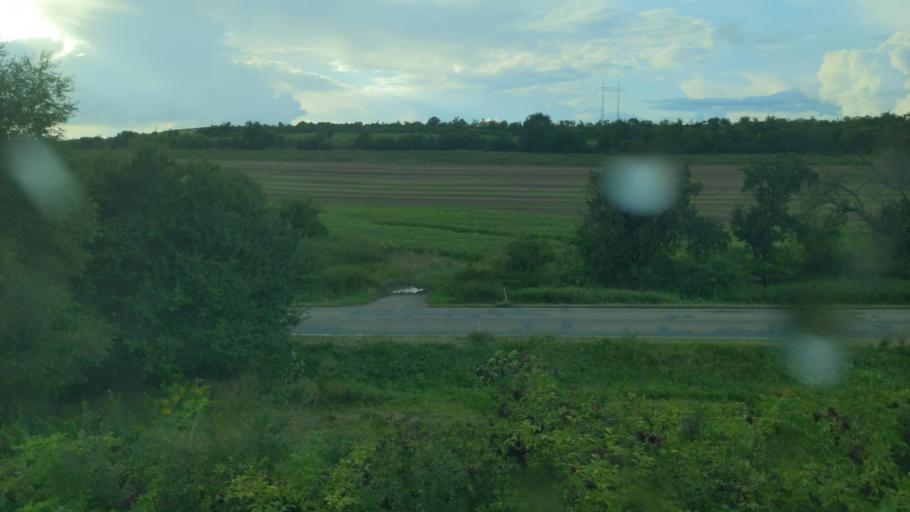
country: CZ
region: Central Bohemia
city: Poricany
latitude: 50.1015
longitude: 14.9080
